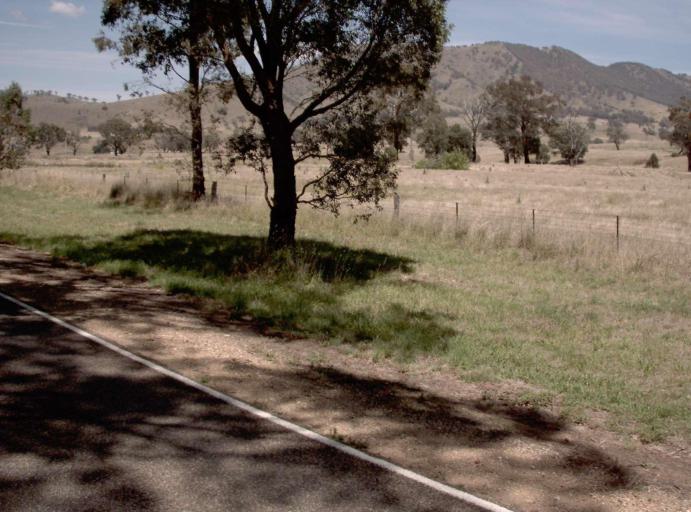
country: AU
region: Victoria
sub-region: East Gippsland
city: Bairnsdale
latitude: -37.2340
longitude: 147.7154
